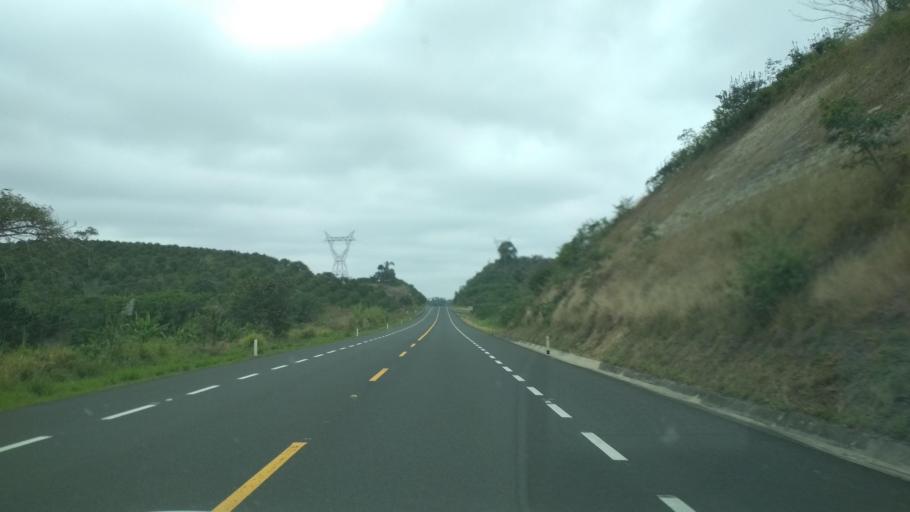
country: MX
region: Veracruz
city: Gutierrez Zamora
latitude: 20.3029
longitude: -97.0915
